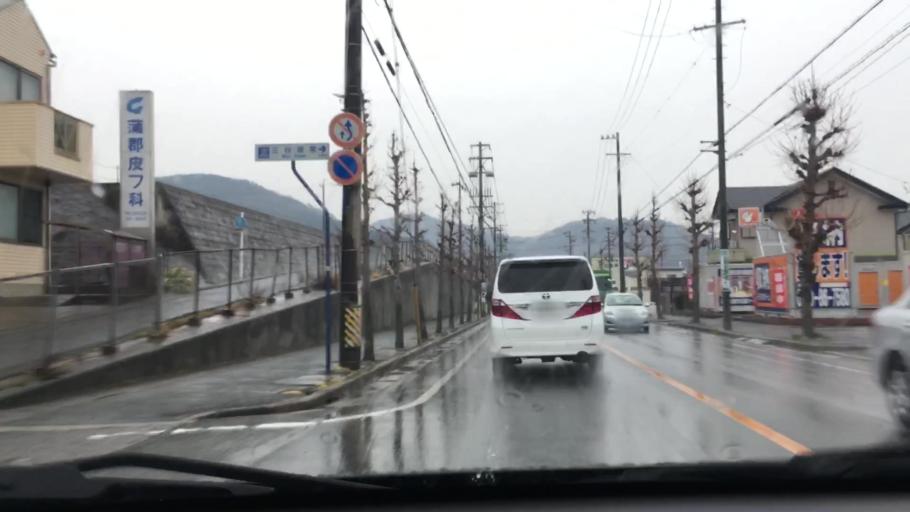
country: JP
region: Aichi
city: Gamagori
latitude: 34.8180
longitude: 137.2535
